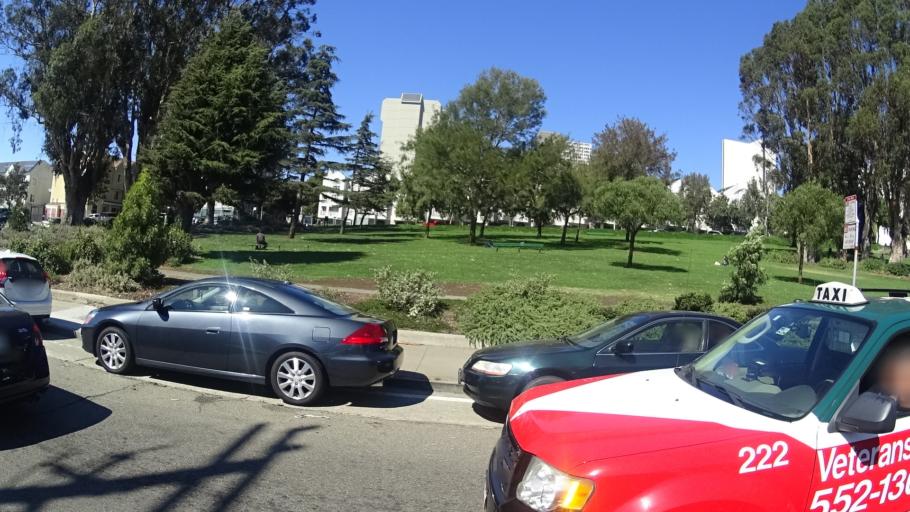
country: US
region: California
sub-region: San Francisco County
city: San Francisco
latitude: 37.7812
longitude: -122.4266
